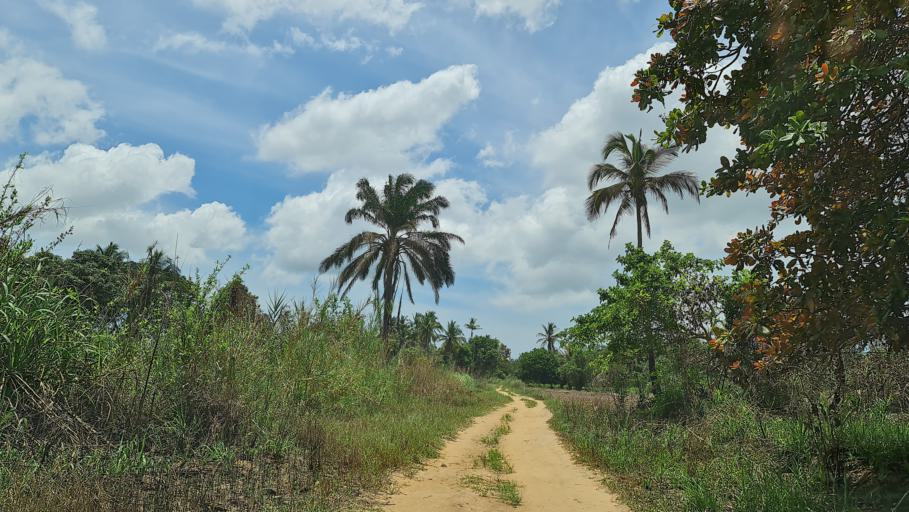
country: MZ
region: Zambezia
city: Quelimane
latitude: -17.5772
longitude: 37.3743
